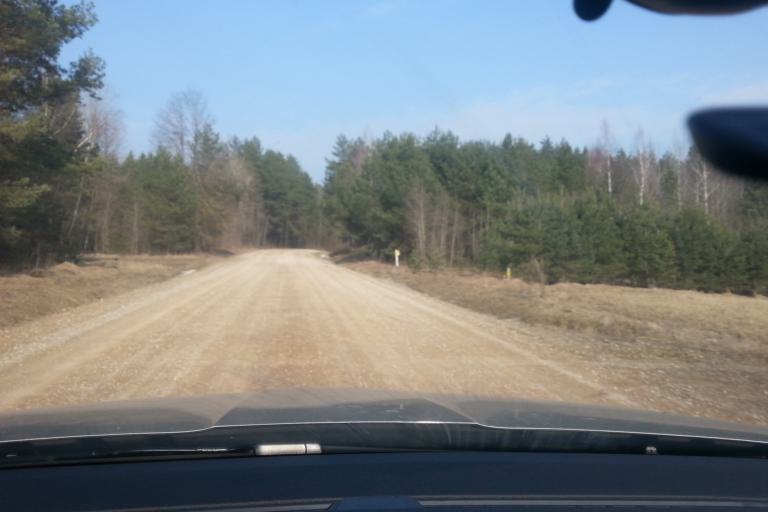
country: LT
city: Trakai
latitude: 54.5741
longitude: 24.9681
